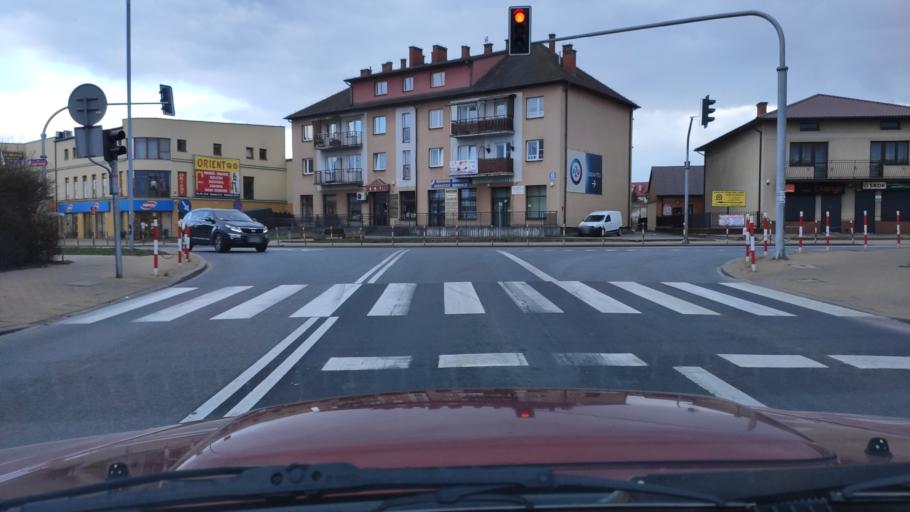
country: PL
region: Masovian Voivodeship
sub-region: Powiat zwolenski
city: Zwolen
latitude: 51.3577
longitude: 21.5823
